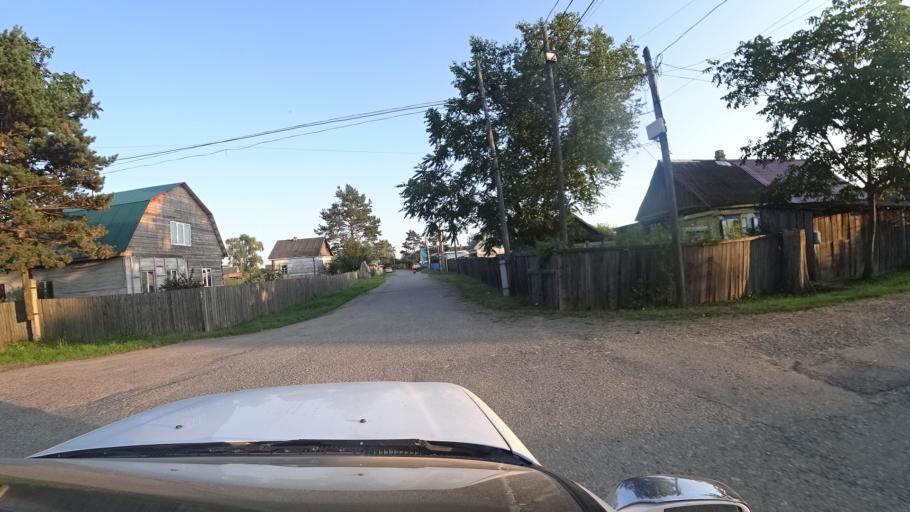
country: RU
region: Primorskiy
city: Dal'nerechensk
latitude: 45.9431
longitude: 133.7558
